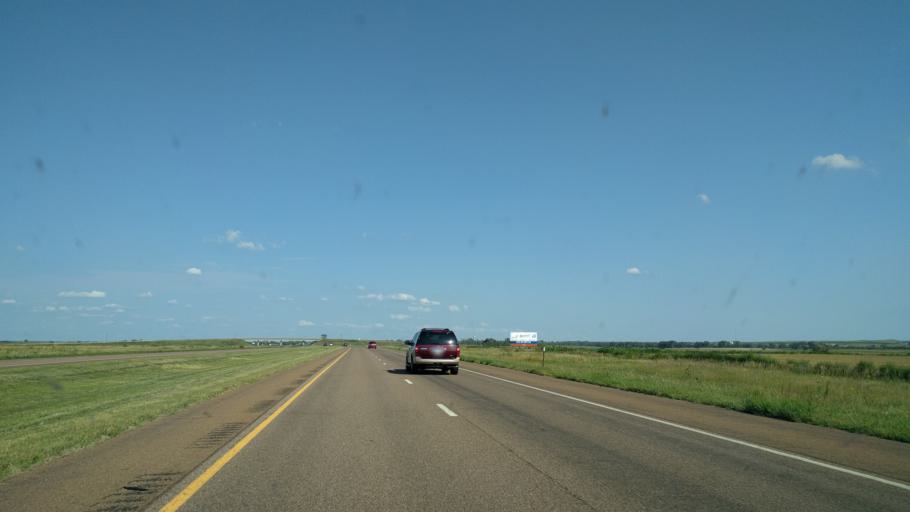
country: US
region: Kansas
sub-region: Ellis County
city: Ellis
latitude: 38.9521
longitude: -99.6022
